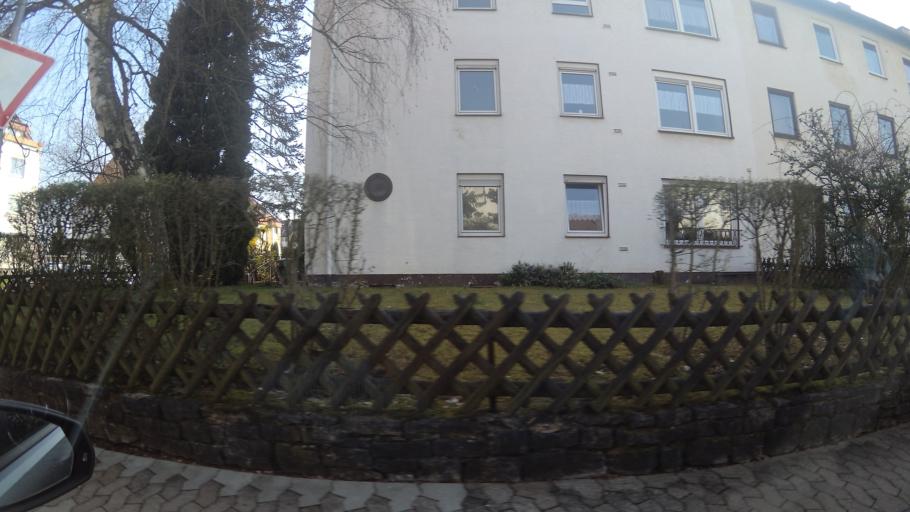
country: DE
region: Saarland
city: Saarbrucken
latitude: 49.2484
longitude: 6.9961
